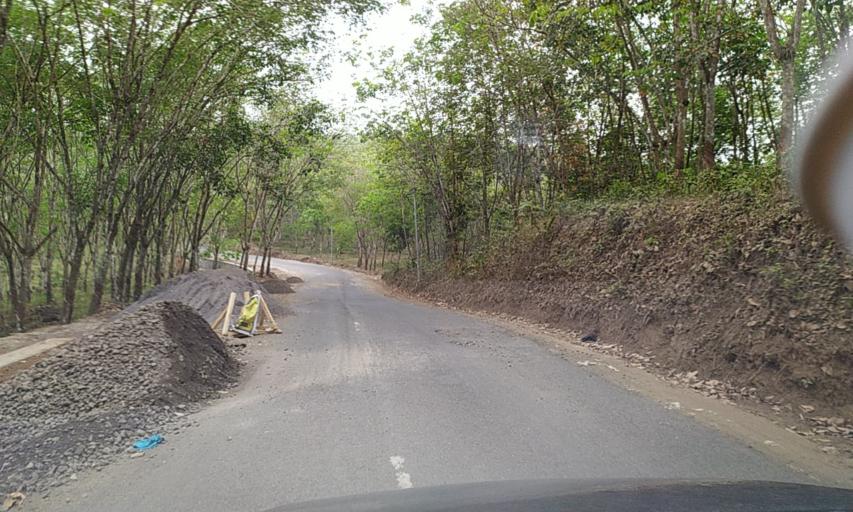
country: ID
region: Central Java
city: Cigalumpit
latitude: -7.3172
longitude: 108.5991
